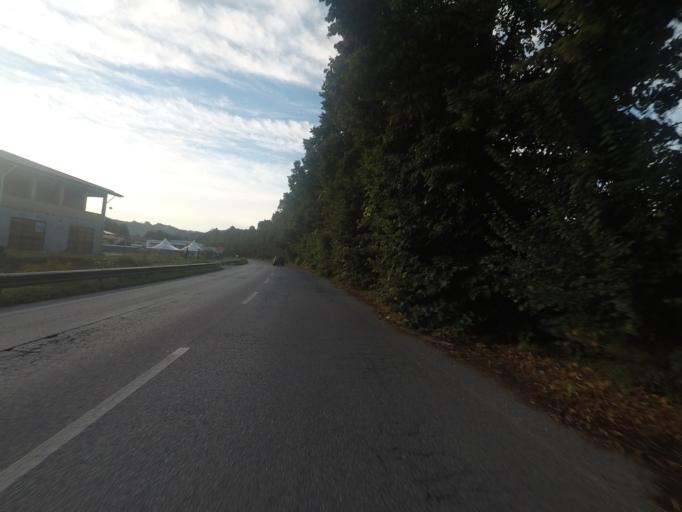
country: IT
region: Tuscany
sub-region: Provincia di Lucca
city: Corsanico-Bargecchia
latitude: 43.9306
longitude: 10.3116
